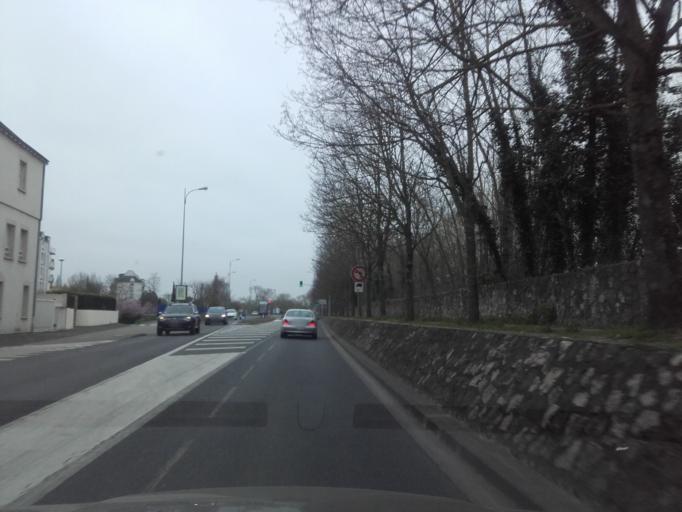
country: FR
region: Centre
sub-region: Departement d'Indre-et-Loire
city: Saint-Cyr-sur-Loire
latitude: 47.3939
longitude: 0.6651
